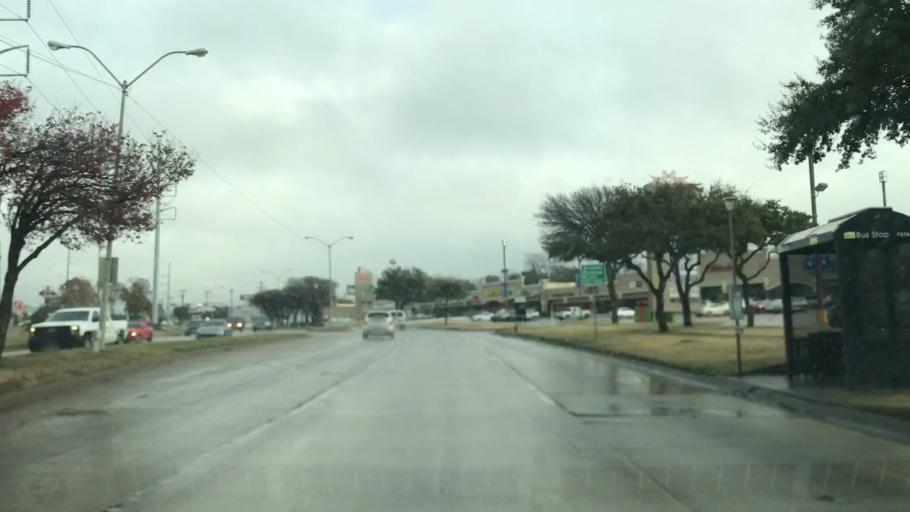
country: US
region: Texas
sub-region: Dallas County
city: Irving
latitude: 32.8415
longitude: -96.9930
